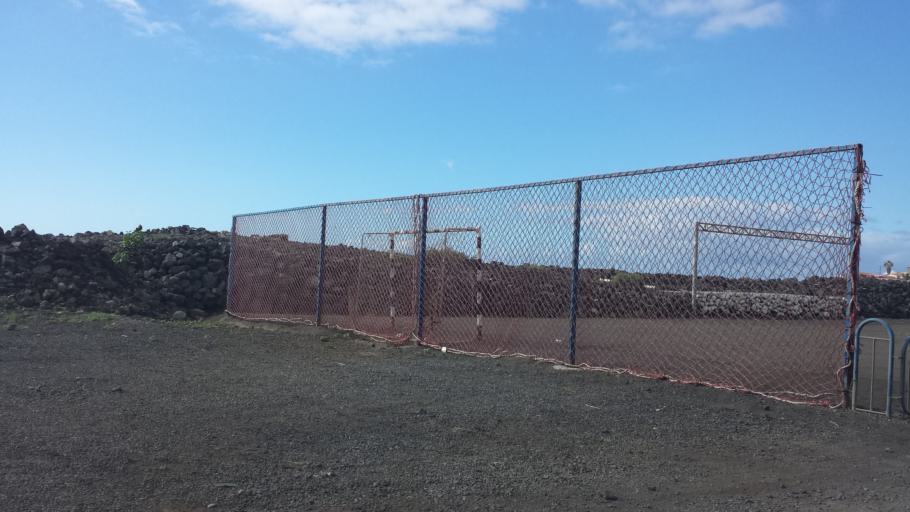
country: ES
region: Canary Islands
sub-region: Provincia de Santa Cruz de Tenerife
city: Fuencaliente de la Palma
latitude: 28.5523
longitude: -17.8885
